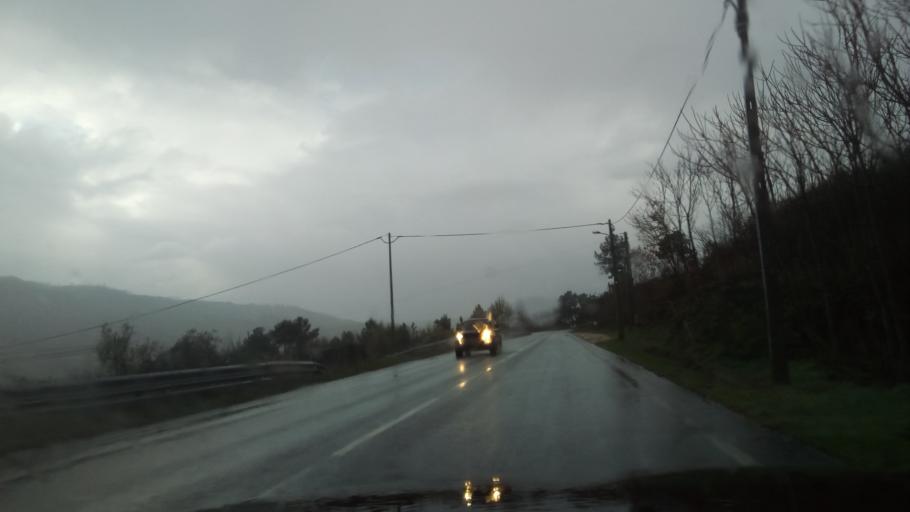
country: PT
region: Guarda
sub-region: Guarda
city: Guarda
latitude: 40.5723
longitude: -7.2971
